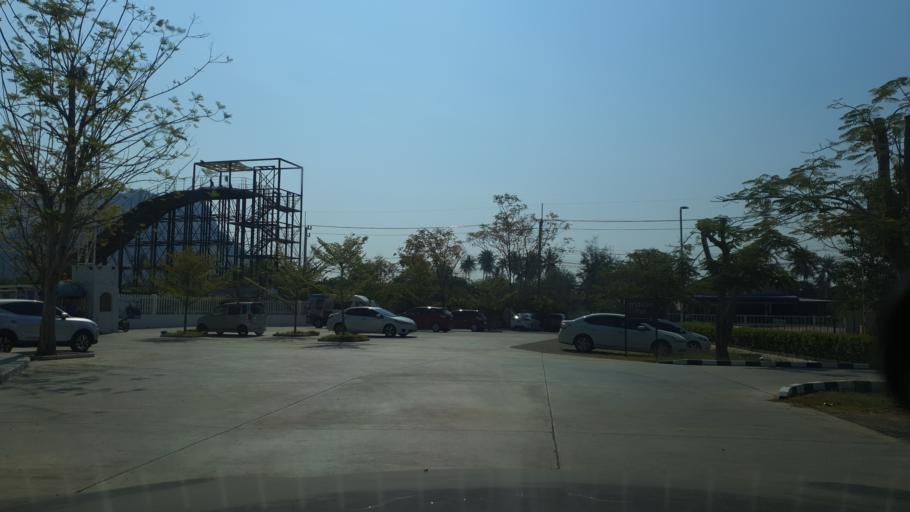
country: TH
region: Phetchaburi
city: Cha-am
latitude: 12.8304
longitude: 99.9325
